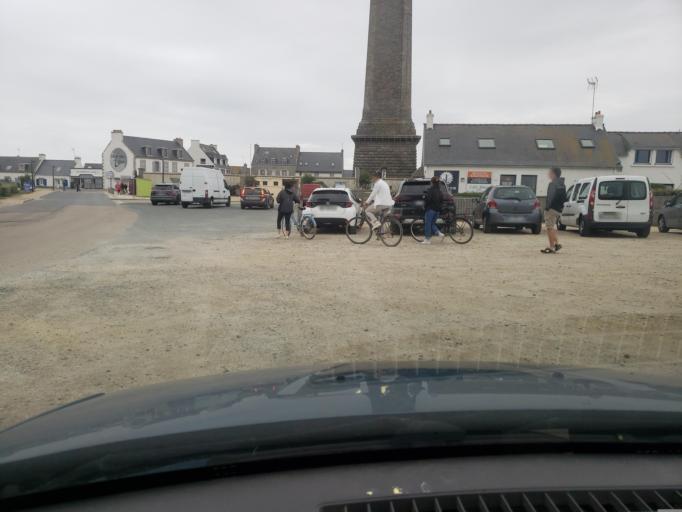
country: FR
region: Brittany
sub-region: Departement du Finistere
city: Guilvinec
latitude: 47.7991
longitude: -4.3732
